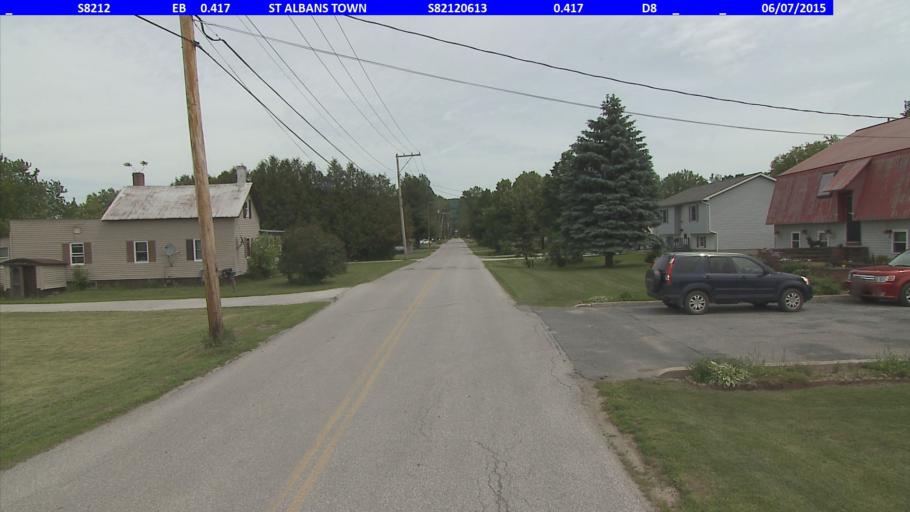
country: US
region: Vermont
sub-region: Franklin County
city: Saint Albans
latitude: 44.8164
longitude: -73.0995
